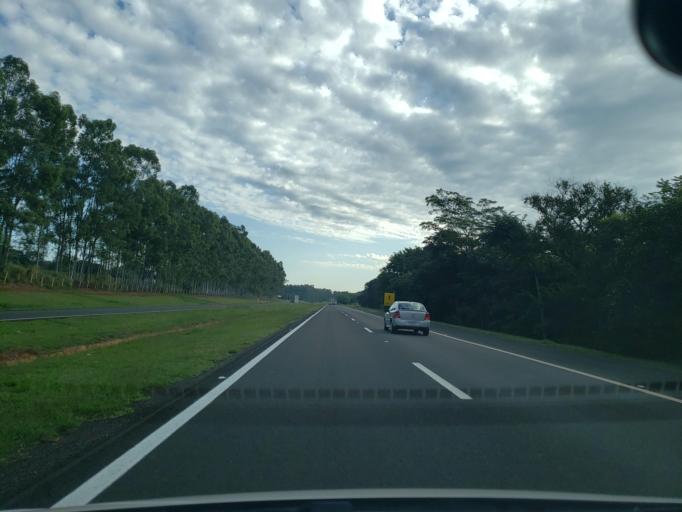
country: BR
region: Sao Paulo
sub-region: Guararapes
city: Guararapes
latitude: -21.2123
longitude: -50.6781
